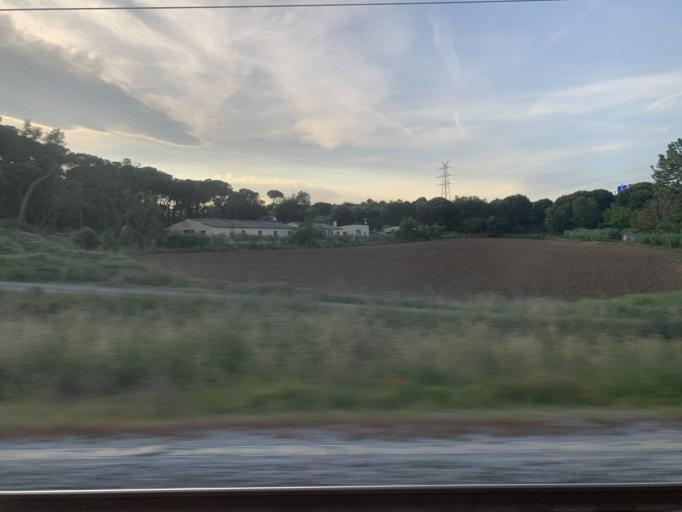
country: ES
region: Catalonia
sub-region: Provincia de Barcelona
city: La Roca del Valles
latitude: 41.5967
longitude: 2.3277
